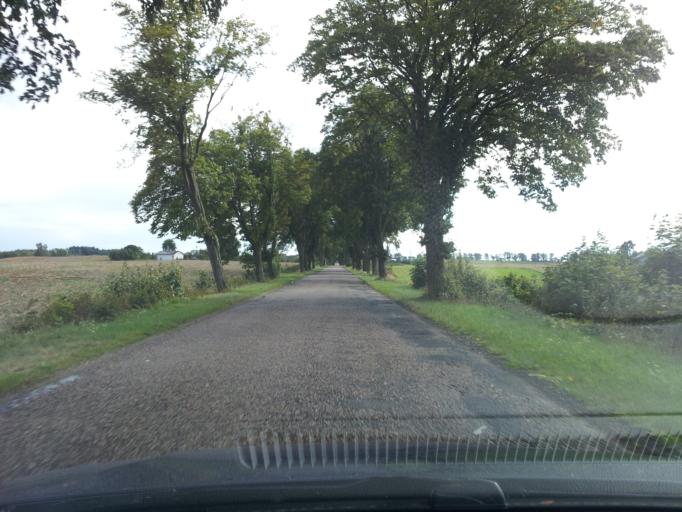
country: PL
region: Kujawsko-Pomorskie
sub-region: Powiat brodnicki
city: Gorzno
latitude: 53.2202
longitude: 19.6343
